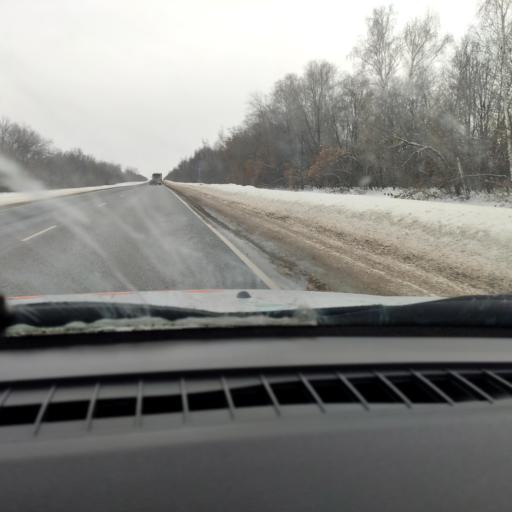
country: RU
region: Samara
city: Dubovyy Umet
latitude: 52.9941
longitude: 50.2577
